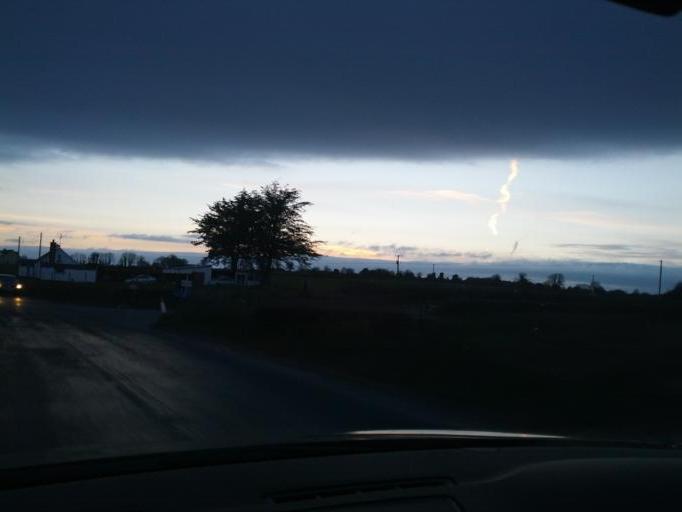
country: IE
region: Connaught
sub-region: County Galway
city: Portumna
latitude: 53.1070
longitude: -8.1293
